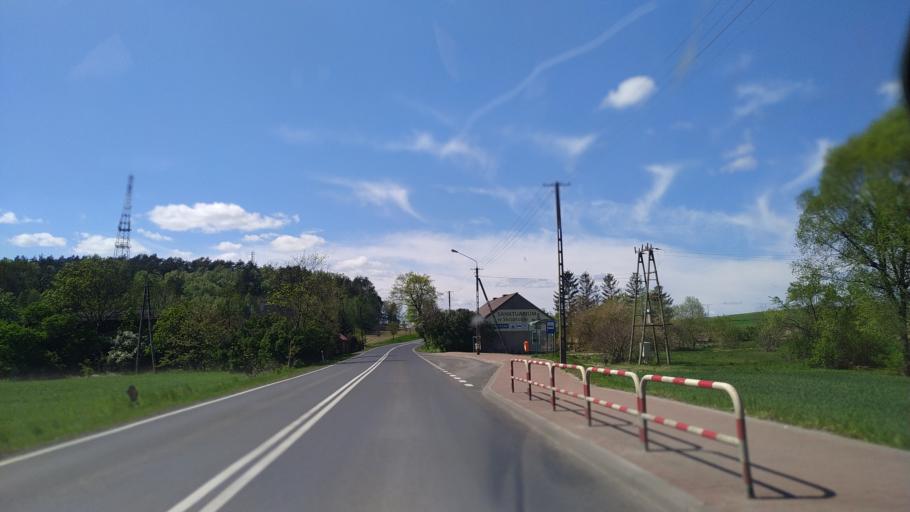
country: PL
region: Greater Poland Voivodeship
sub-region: Powiat pilski
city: Szydlowo
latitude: 53.2401
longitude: 16.6394
